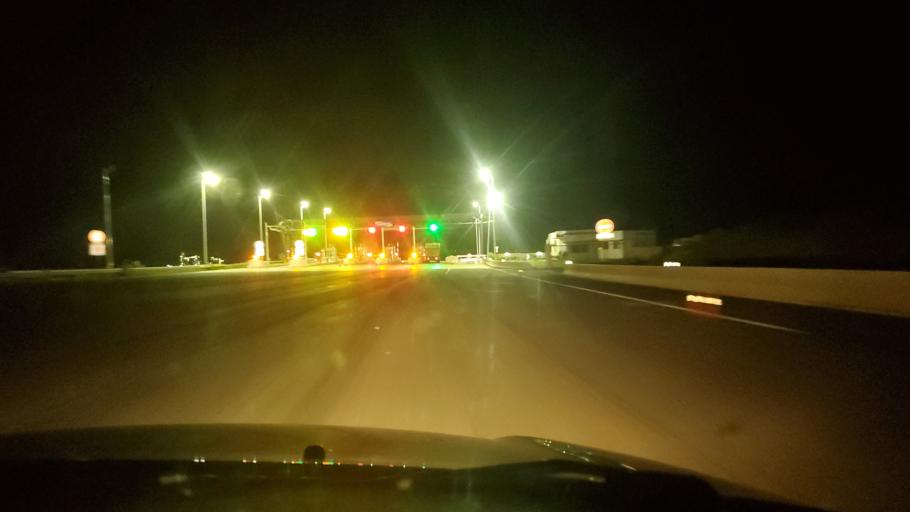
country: SN
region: Thies
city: Pout
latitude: 14.6986
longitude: -17.0413
